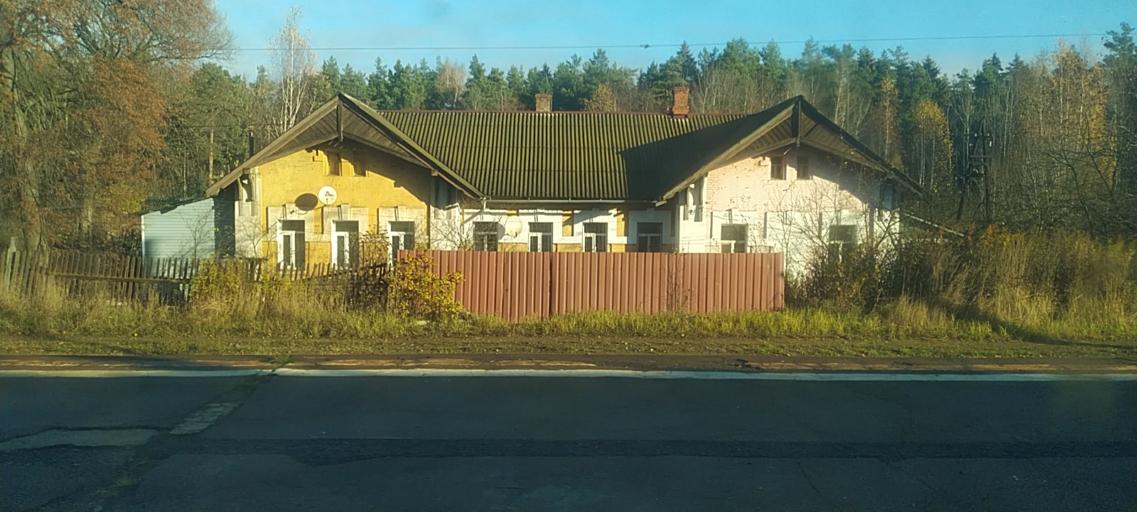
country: RU
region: Moskovskaya
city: Ramenskoye
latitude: 55.6361
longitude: 38.2753
